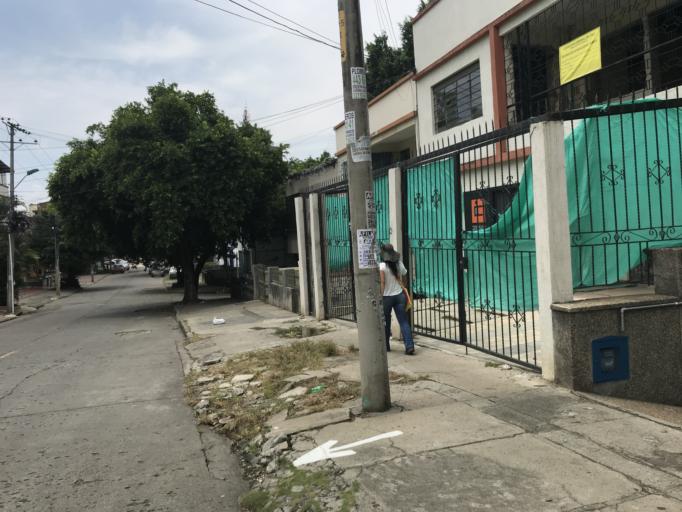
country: CO
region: Valle del Cauca
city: Cali
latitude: 3.4391
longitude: -76.5392
